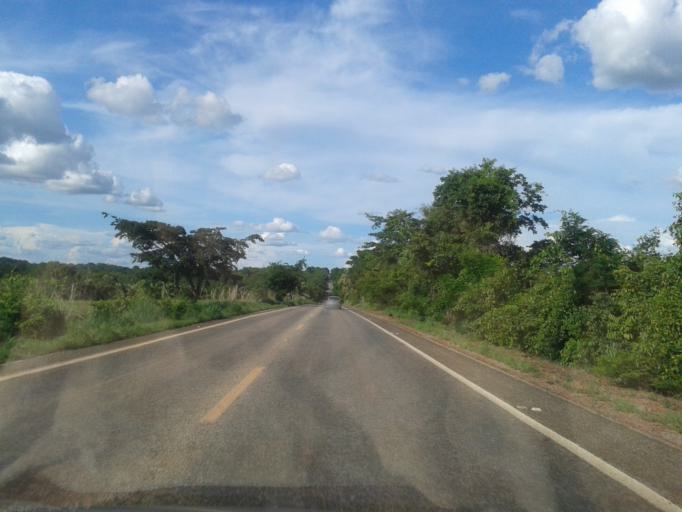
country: BR
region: Goias
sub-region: Mozarlandia
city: Mozarlandia
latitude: -14.4614
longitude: -50.4665
